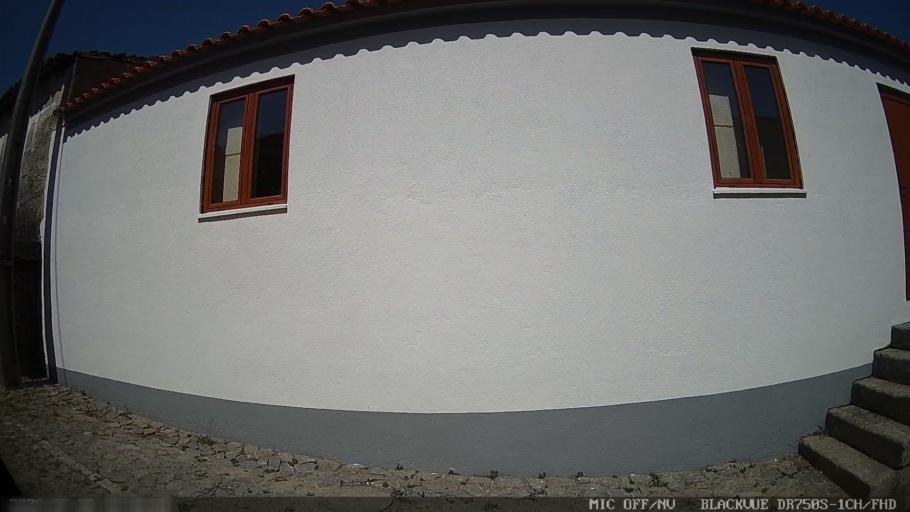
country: PT
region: Vila Real
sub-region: Murca
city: Murca
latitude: 41.3279
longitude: -7.4889
